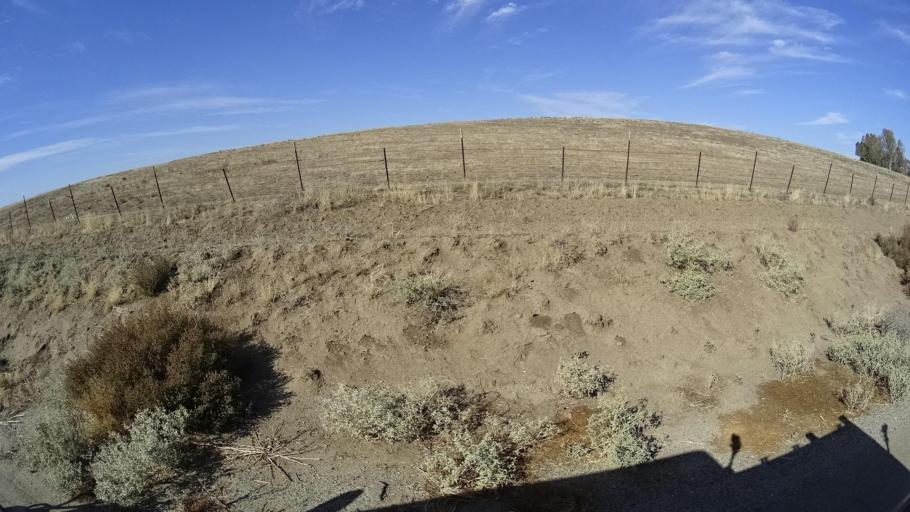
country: US
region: California
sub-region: Tulare County
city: Richgrove
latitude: 35.6305
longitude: -118.9718
